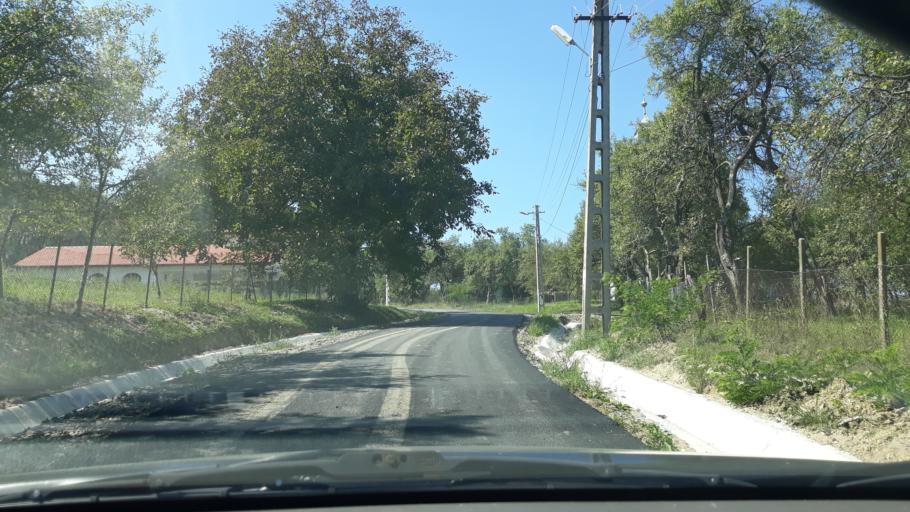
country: RO
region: Salaj
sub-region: Comuna Dobrin
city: Dobrin
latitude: 47.2947
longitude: 23.0883
